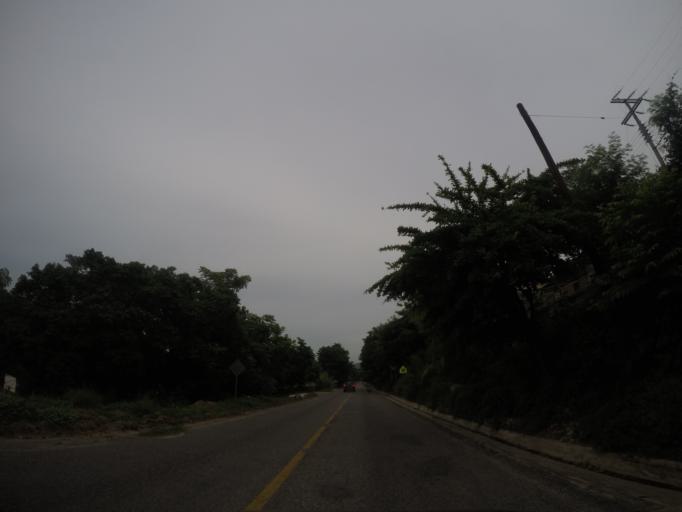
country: MX
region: Oaxaca
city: San Pedro Mixtepec
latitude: 15.9471
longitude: -97.1868
